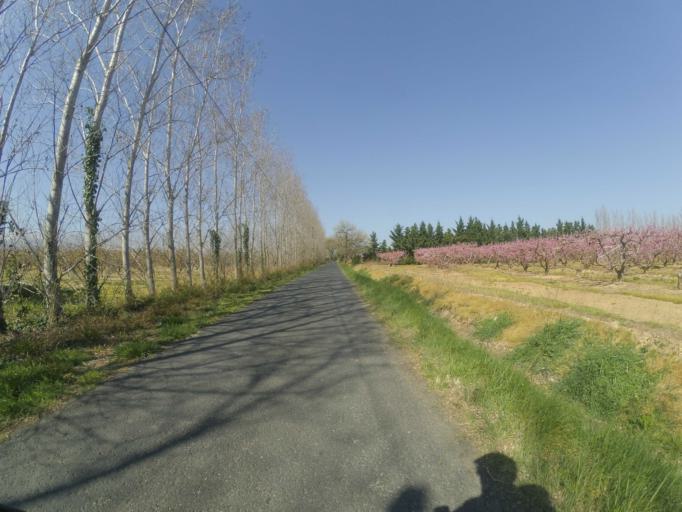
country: FR
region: Languedoc-Roussillon
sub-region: Departement des Pyrenees-Orientales
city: Thuir
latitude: 42.6535
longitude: 2.7636
